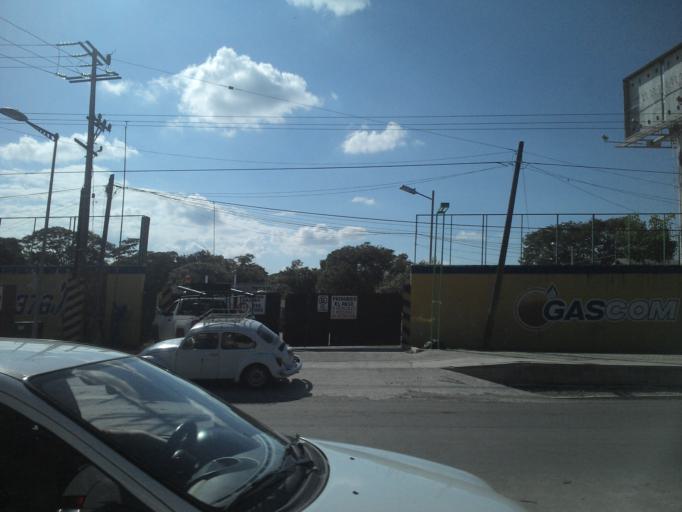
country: MX
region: Chiapas
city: Palenque
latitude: 17.5225
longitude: -91.9928
